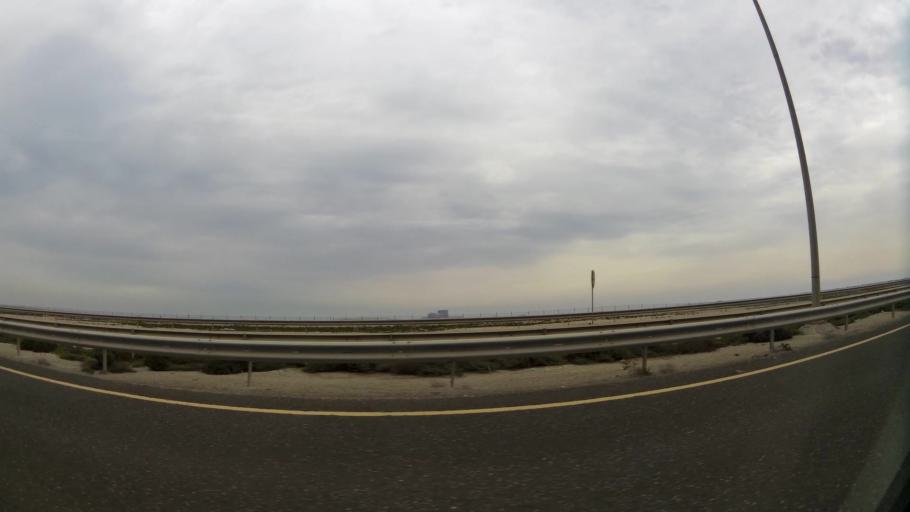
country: BH
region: Central Governorate
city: Dar Kulayb
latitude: 25.8639
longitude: 50.5845
